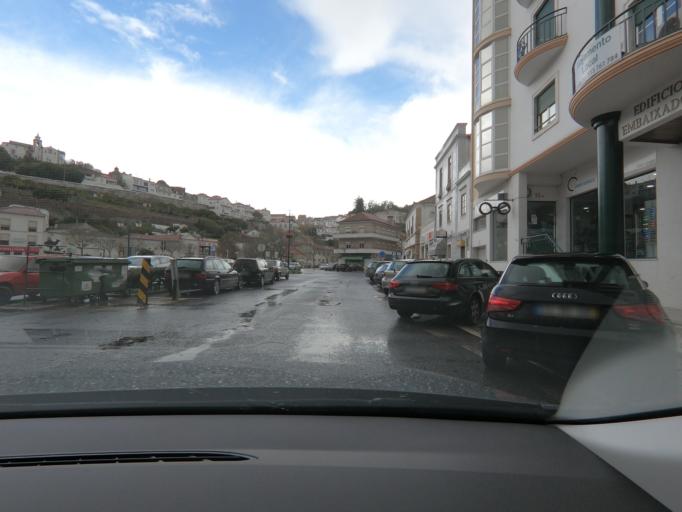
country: PT
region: Lisbon
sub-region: Alenquer
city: Alenquer
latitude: 39.0521
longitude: -9.0081
